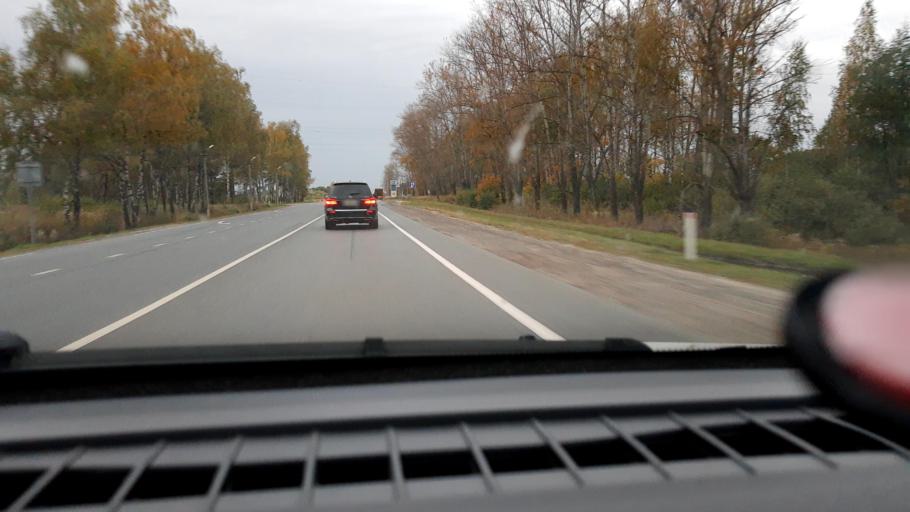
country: RU
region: Vladimir
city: Orgtrud
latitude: 56.2100
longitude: 40.6031
